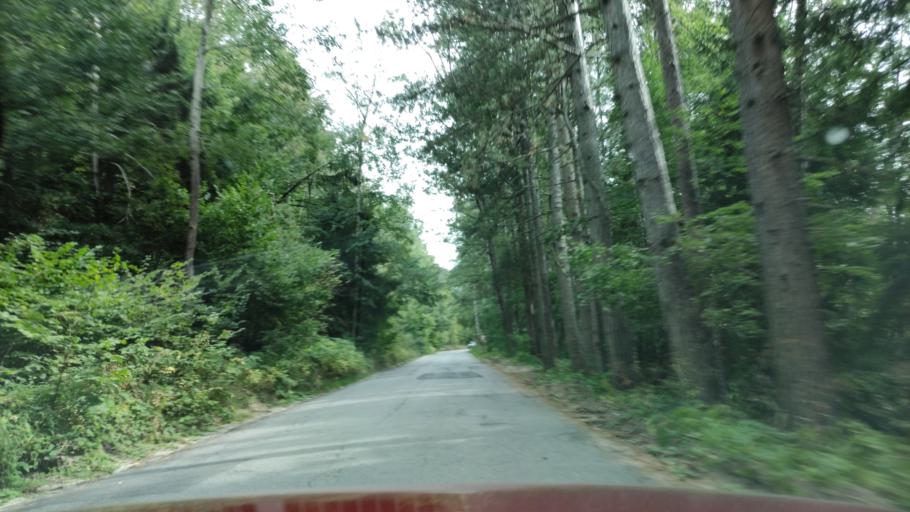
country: BG
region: Sofia-Capital
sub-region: Stolichna Obshtina
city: Sofia
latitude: 42.6149
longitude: 23.2317
